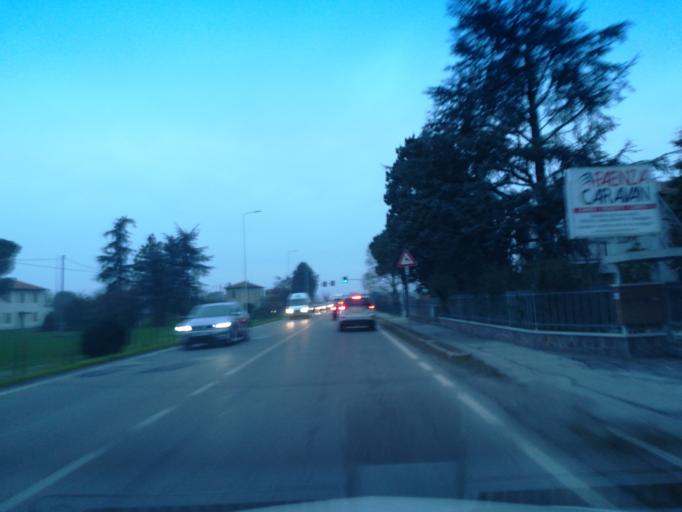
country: IT
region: Emilia-Romagna
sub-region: Provincia di Ravenna
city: Faenza
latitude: 44.3026
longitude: 11.8418
